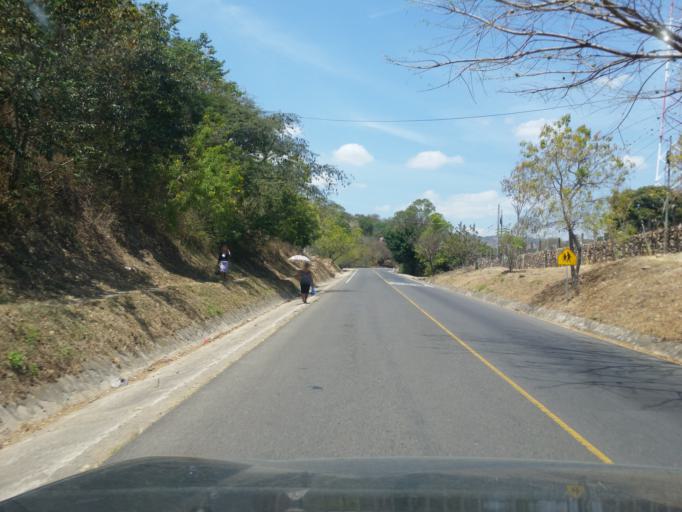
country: NI
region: Esteli
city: Esteli
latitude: 12.9957
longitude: -86.2964
